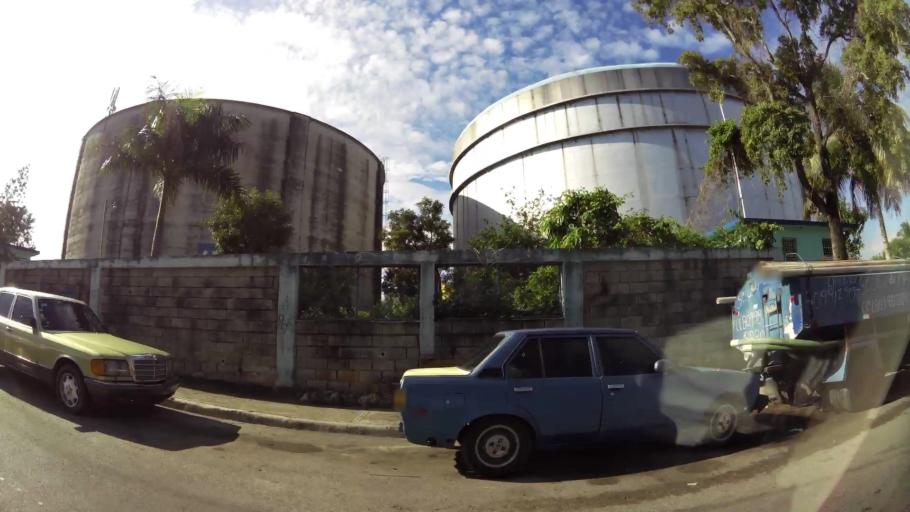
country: DO
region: Santo Domingo
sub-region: Santo Domingo
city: Santo Domingo Este
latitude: 18.4869
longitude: -69.8628
